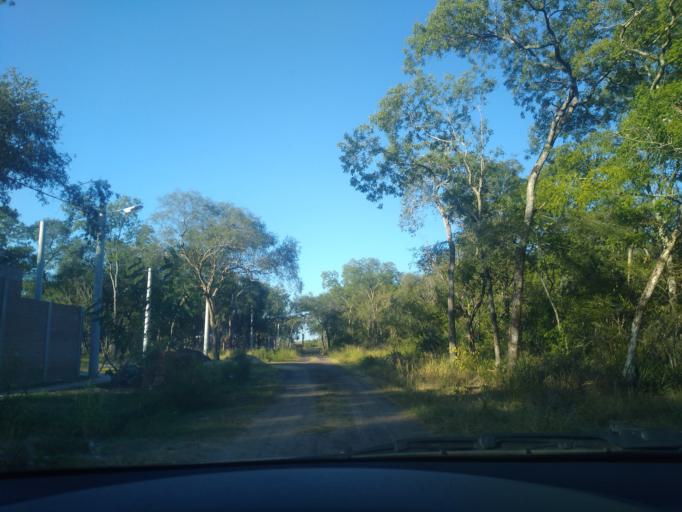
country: AR
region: Chaco
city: Resistencia
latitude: -27.4109
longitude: -58.9531
